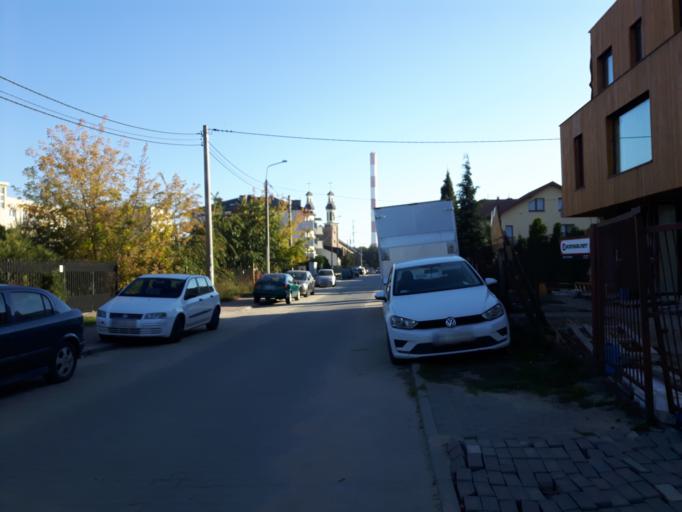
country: PL
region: Masovian Voivodeship
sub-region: Powiat wolominski
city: Zabki
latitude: 52.2809
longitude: 21.1252
